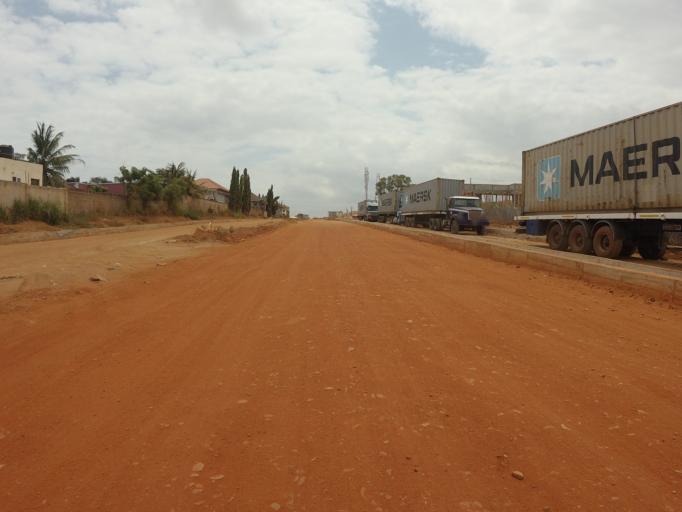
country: GH
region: Greater Accra
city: Medina Estates
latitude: 5.6284
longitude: -0.1447
